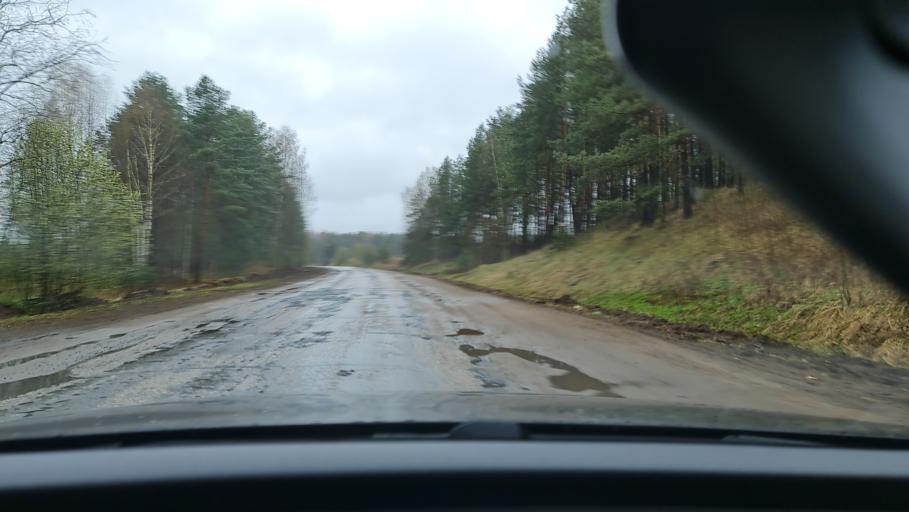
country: RU
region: Novgorod
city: Valday
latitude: 58.0405
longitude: 32.9234
